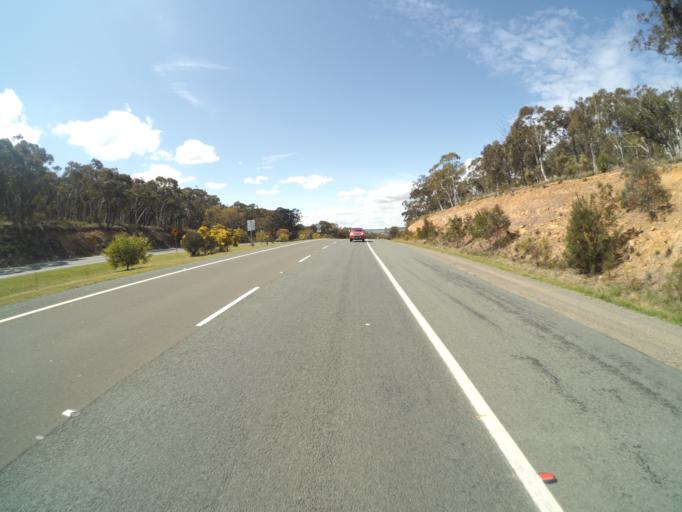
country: AU
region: New South Wales
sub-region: Goulburn Mulwaree
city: Goulburn
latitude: -34.7420
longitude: 149.7600
